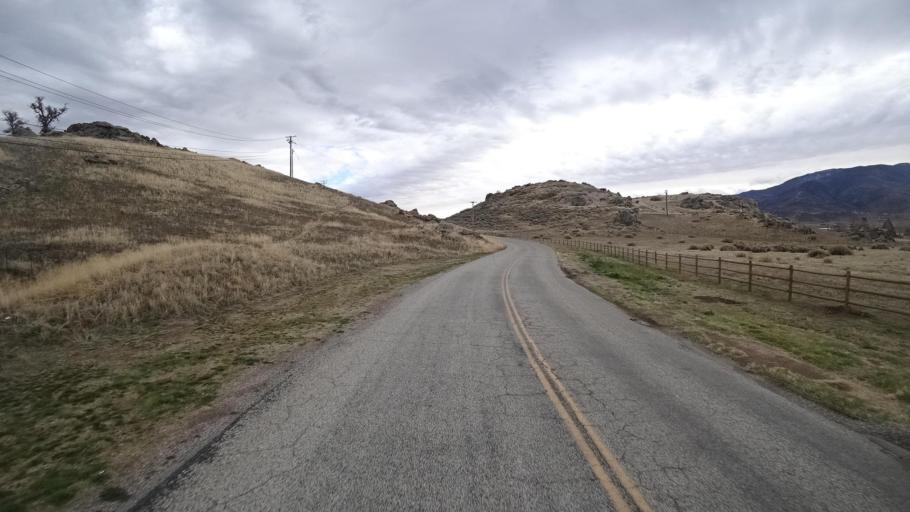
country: US
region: California
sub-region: Kern County
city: Bear Valley Springs
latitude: 35.1235
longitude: -118.6163
